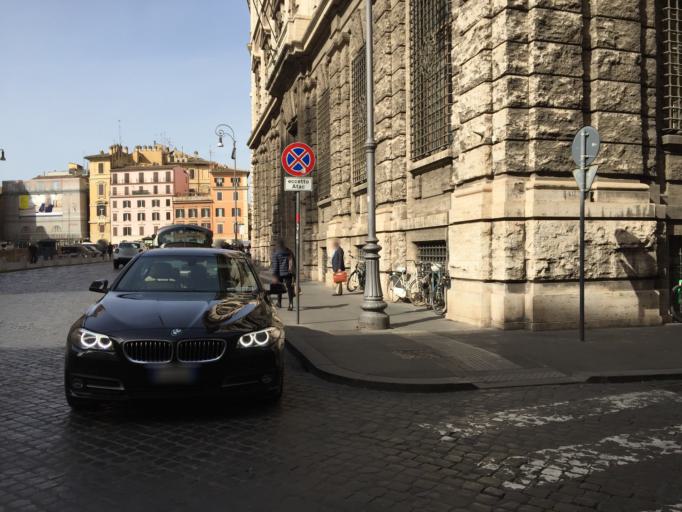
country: VA
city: Vatican City
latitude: 41.9024
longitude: 12.4793
